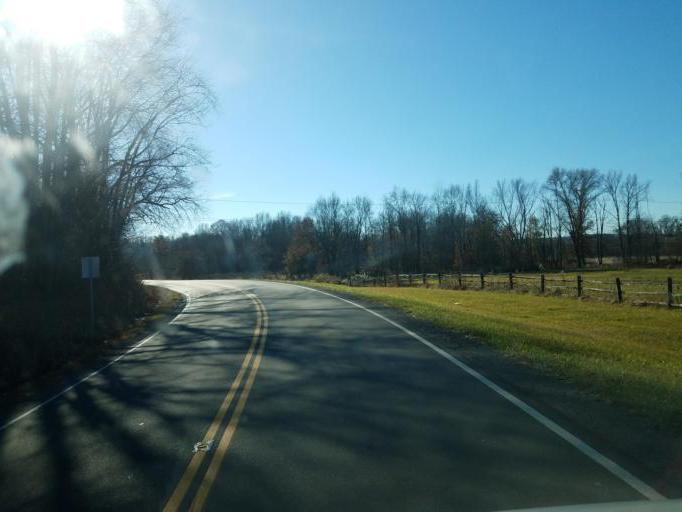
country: US
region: Ohio
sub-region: Muskingum County
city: Dresden
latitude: 40.1622
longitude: -82.0260
